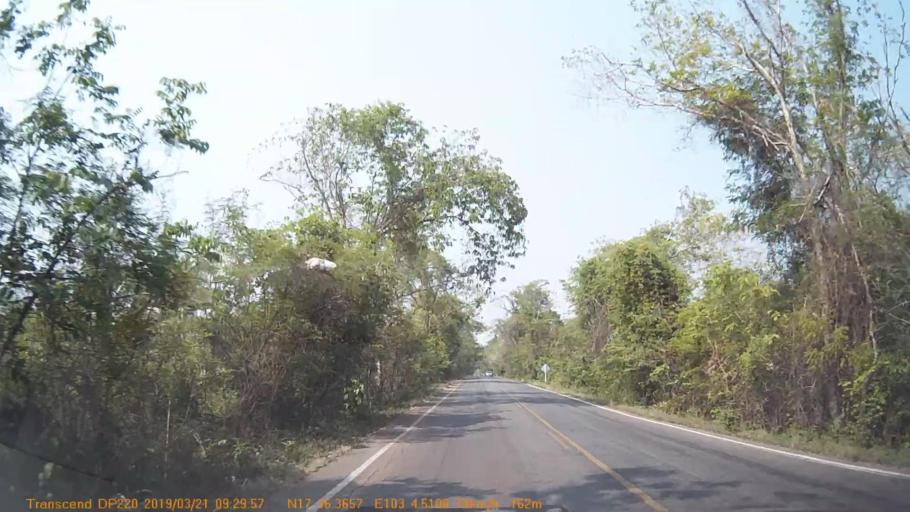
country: TH
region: Changwat Udon Thani
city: Phibun Rak
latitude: 17.6060
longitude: 103.0750
